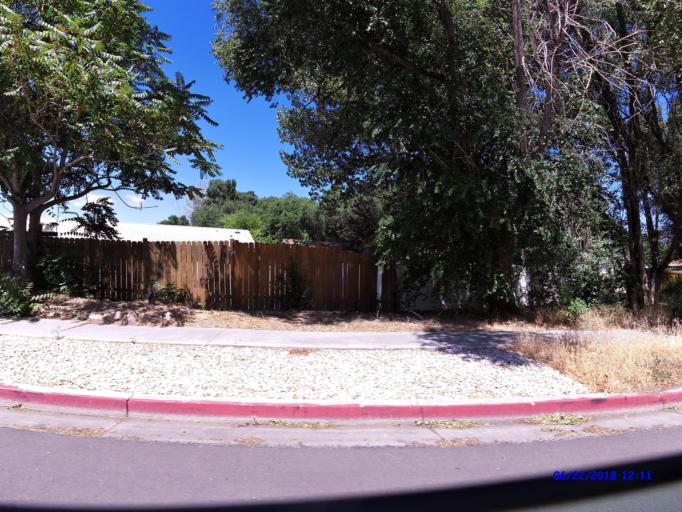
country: US
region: Utah
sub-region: Weber County
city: Ogden
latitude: 41.2371
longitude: -111.9532
